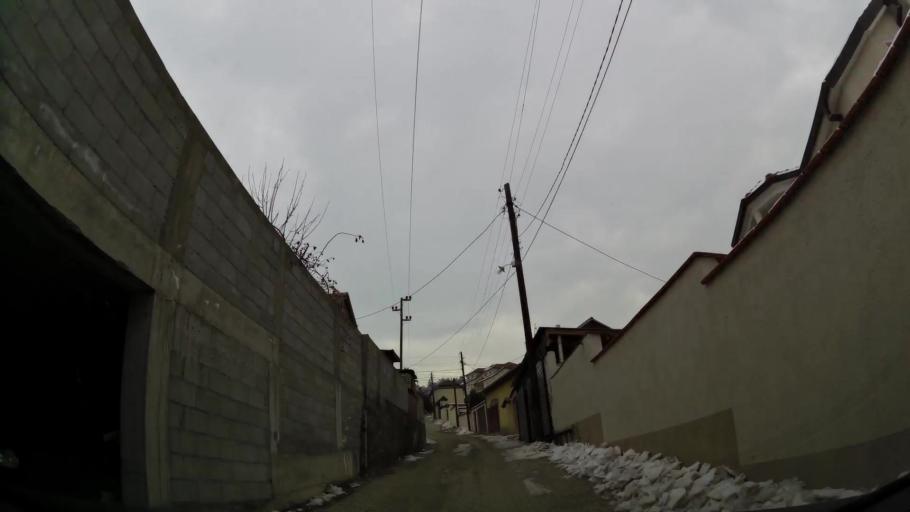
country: MK
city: Kondovo
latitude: 42.0131
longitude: 21.3141
